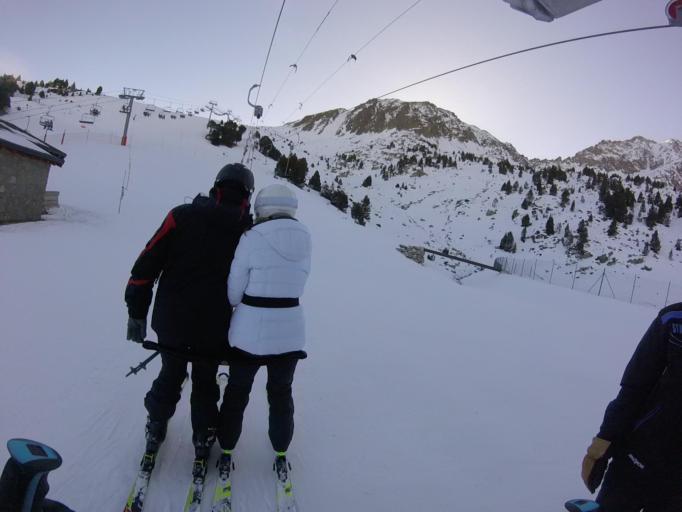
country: AD
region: Canillo
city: El Tarter
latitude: 42.5379
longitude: 1.6755
